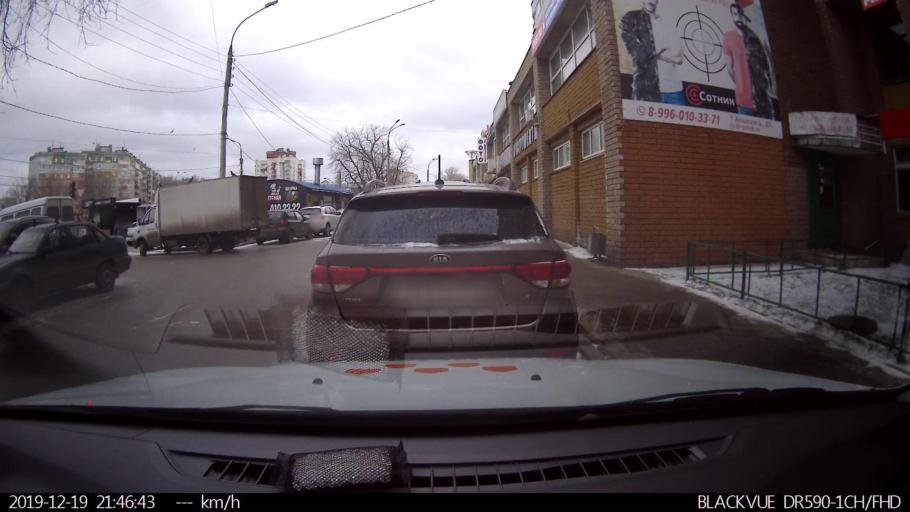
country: RU
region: Nizjnij Novgorod
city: Afonino
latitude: 56.2673
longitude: 44.0625
